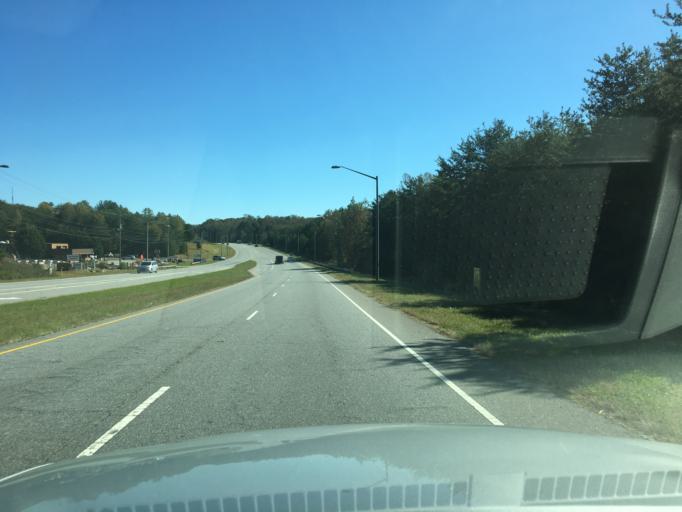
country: US
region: North Carolina
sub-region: Catawba County
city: Saint Stephens
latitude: 35.7205
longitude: -81.2782
